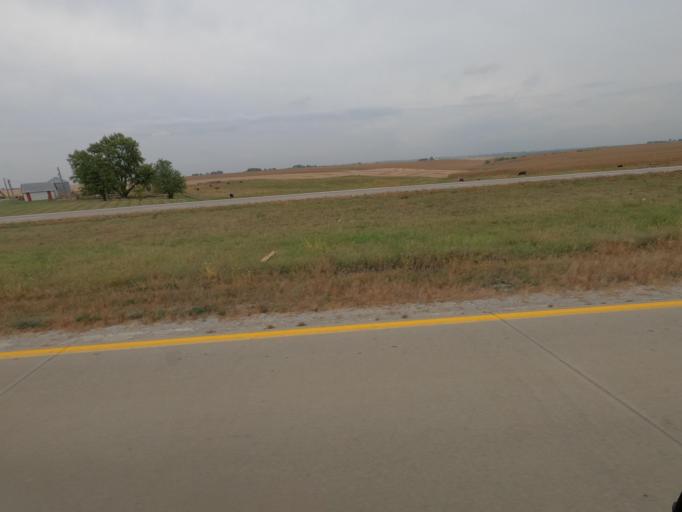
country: US
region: Iowa
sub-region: Marion County
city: Pella
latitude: 41.3657
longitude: -92.7903
